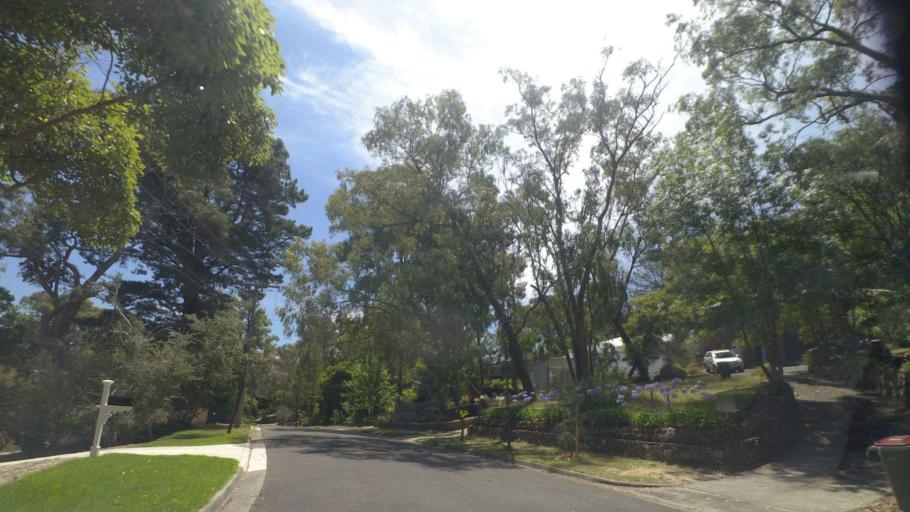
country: AU
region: Victoria
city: Mitcham
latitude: -37.8053
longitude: 145.2214
